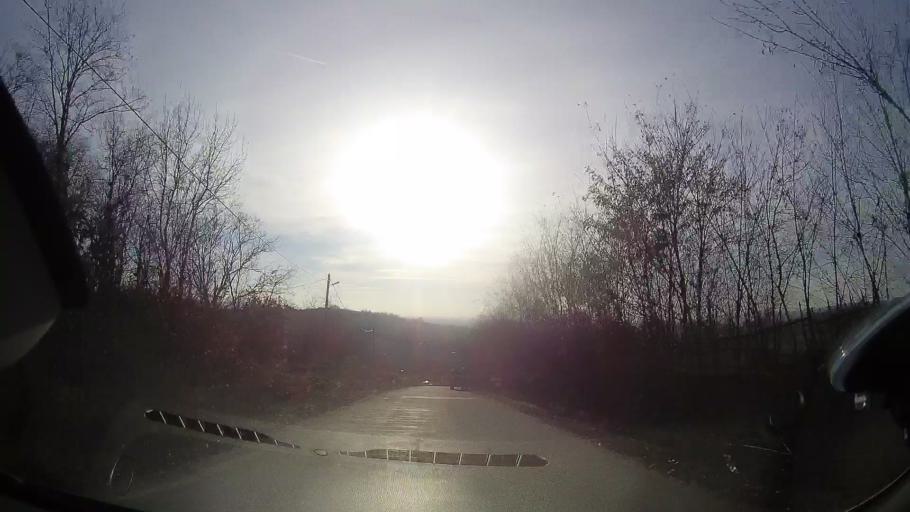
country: RO
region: Bihor
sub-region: Comuna Sarbi
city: Burzuc
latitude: 47.1122
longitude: 22.1783
